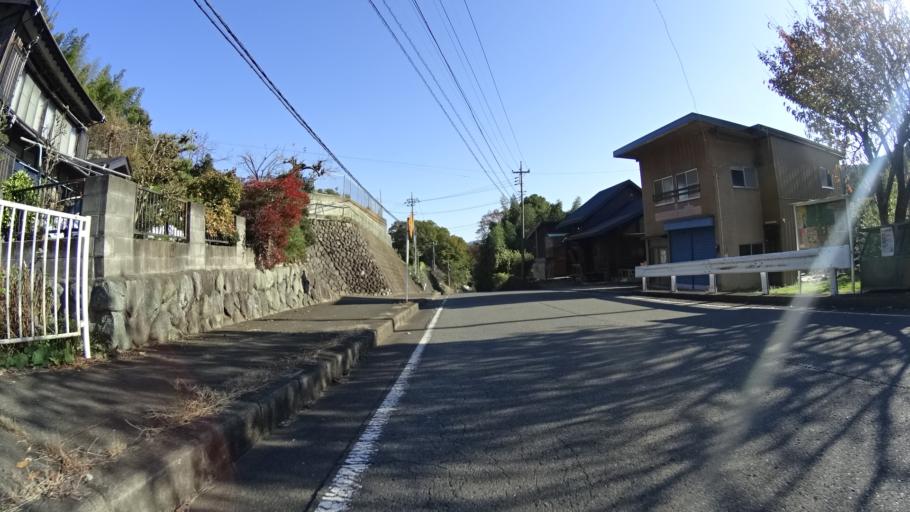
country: JP
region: Yamanashi
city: Uenohara
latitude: 35.6481
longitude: 139.1229
